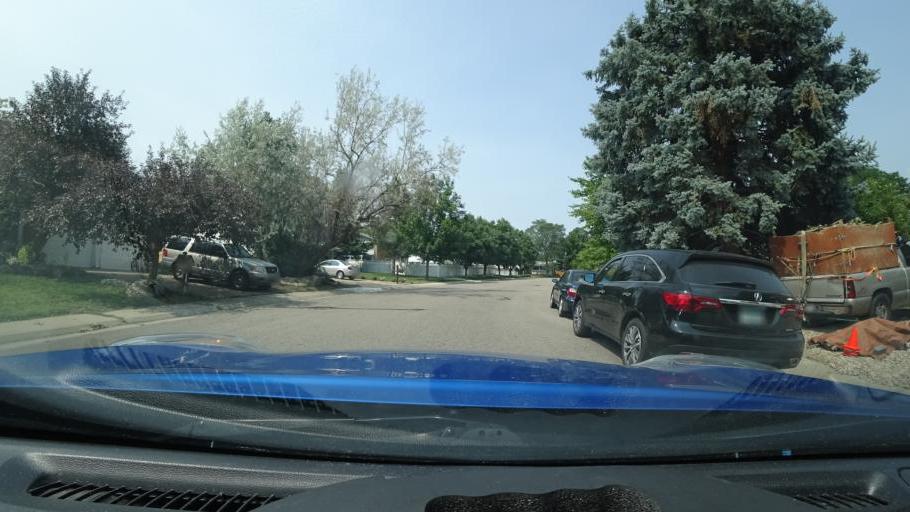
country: US
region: Colorado
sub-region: Adams County
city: Aurora
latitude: 39.6686
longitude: -104.8558
